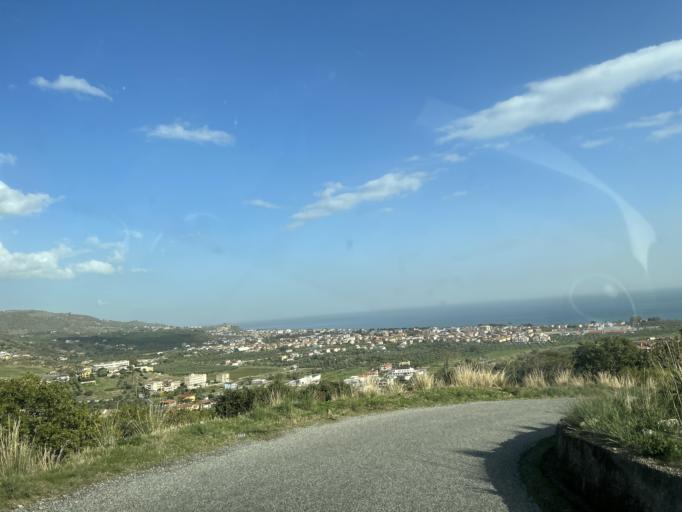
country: IT
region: Calabria
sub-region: Provincia di Catanzaro
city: Montepaone
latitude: 38.7175
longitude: 16.5145
